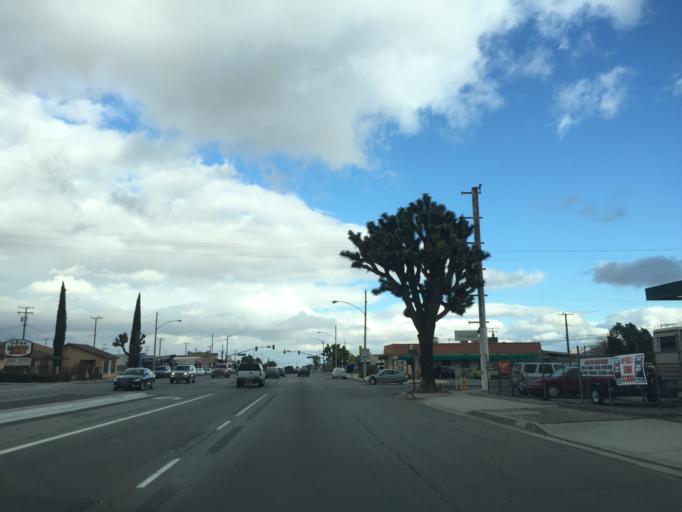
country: US
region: California
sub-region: San Bernardino County
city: Yucca Valley
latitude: 34.1189
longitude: -116.4479
